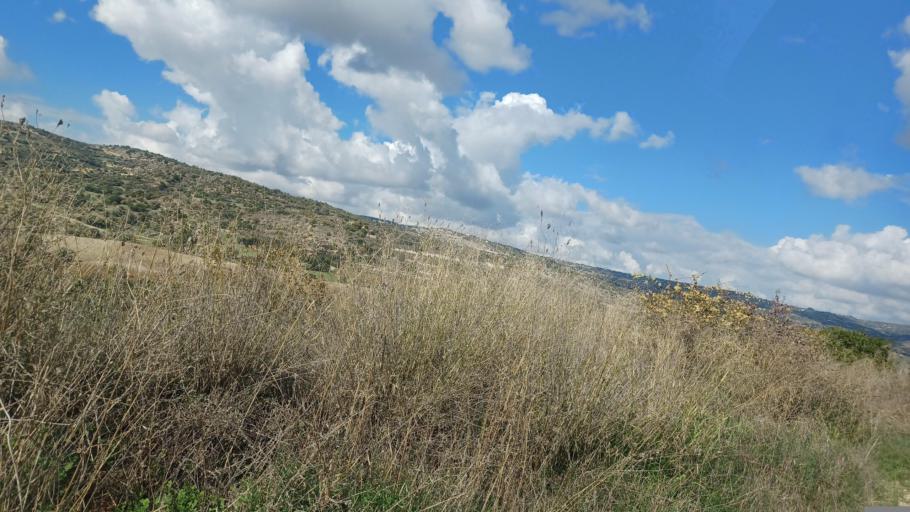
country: CY
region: Pafos
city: Mesogi
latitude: 34.8380
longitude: 32.5464
